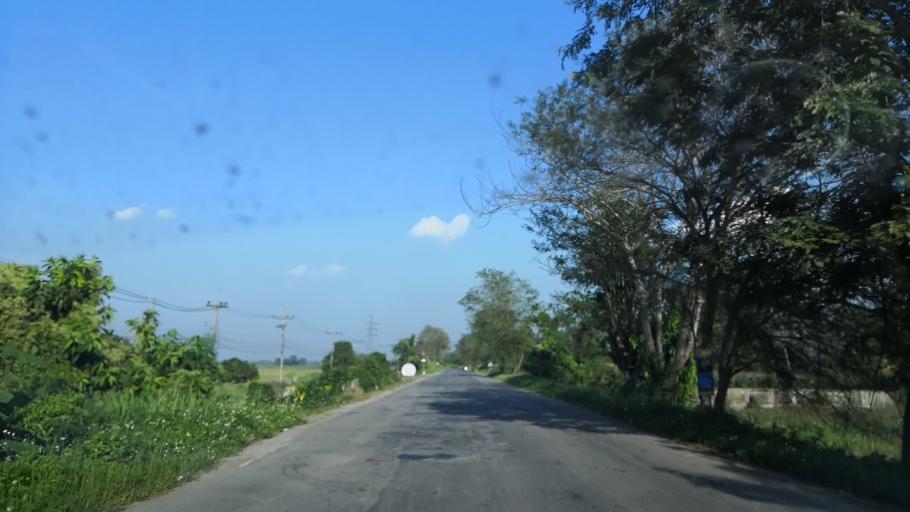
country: TH
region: Chiang Rai
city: Wiang Chai
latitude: 19.9464
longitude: 99.9183
